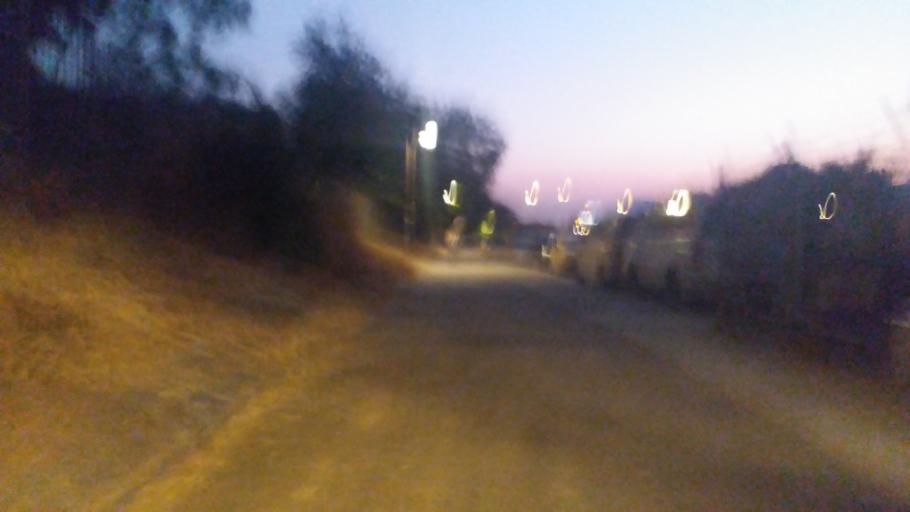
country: HK
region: Yuen Long
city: Yuen Long Kau Hui
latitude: 22.4484
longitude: 113.9985
